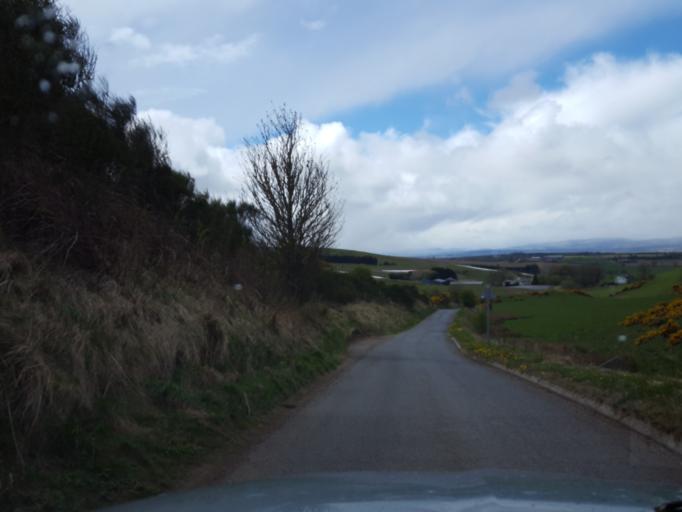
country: GB
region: Scotland
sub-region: Perth and Kinross
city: Scone
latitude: 56.4367
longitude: -3.3120
